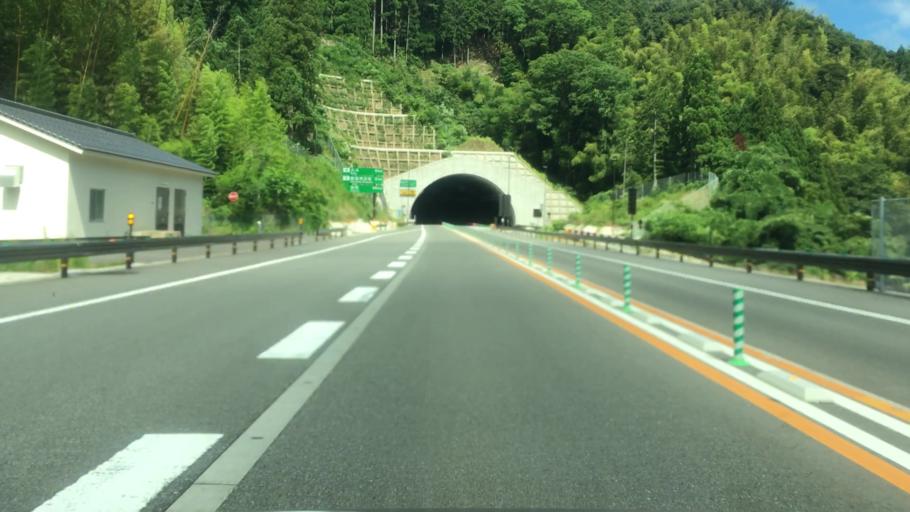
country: JP
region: Hyogo
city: Toyooka
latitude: 35.6390
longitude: 134.5642
